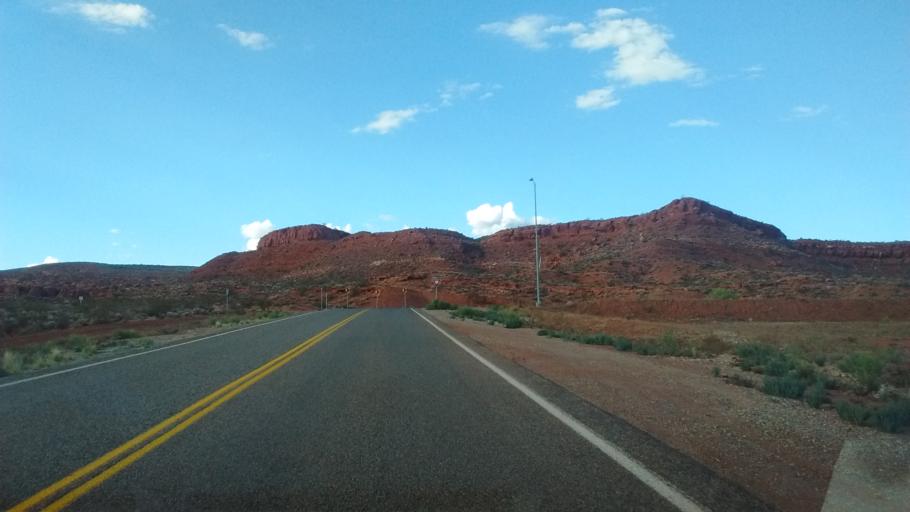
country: US
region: Utah
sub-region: Washington County
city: Washington
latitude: 37.1488
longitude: -113.4921
